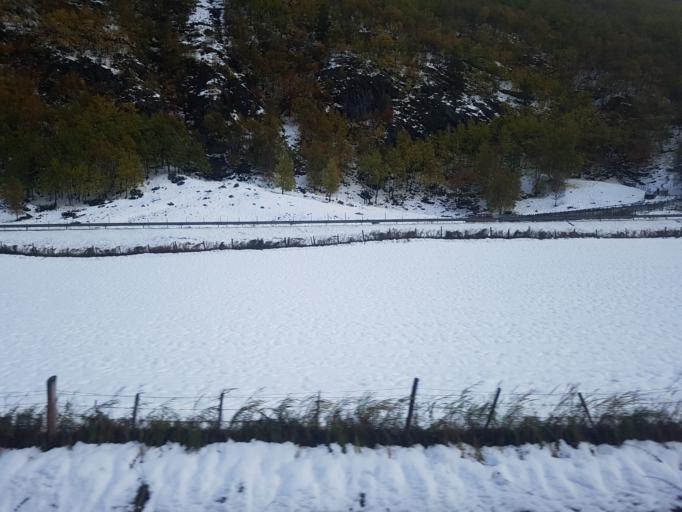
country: NO
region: Sor-Trondelag
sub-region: Oppdal
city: Oppdal
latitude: 62.4179
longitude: 9.6199
